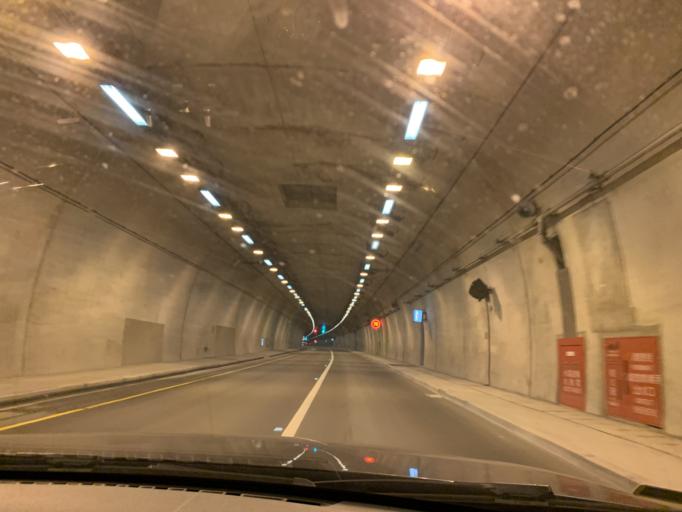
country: TW
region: Taiwan
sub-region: Yilan
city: Yilan
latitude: 24.5346
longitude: 121.8358
